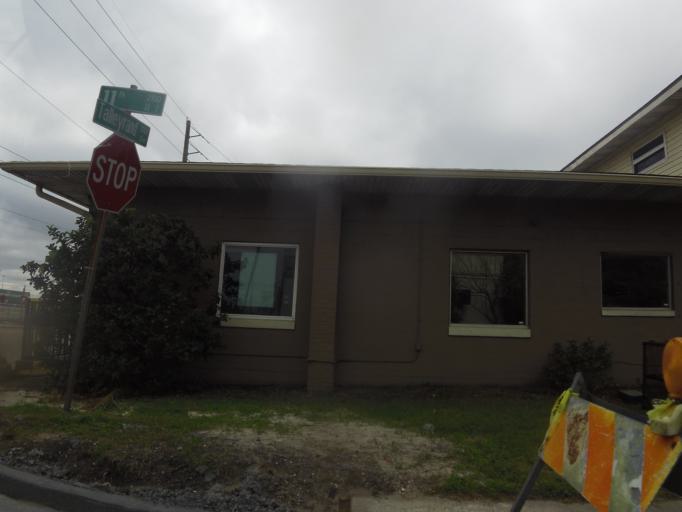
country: US
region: Florida
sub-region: Duval County
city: Jacksonville
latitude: 30.3498
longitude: -81.6260
